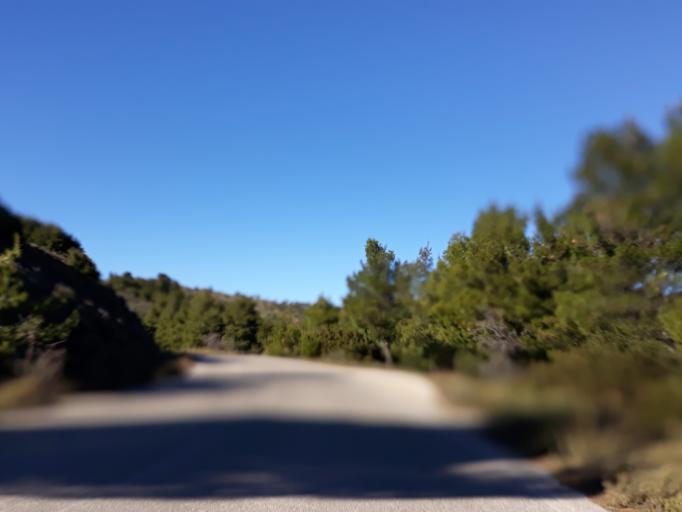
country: GR
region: Attica
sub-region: Nomarchia Dytikis Attikis
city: Fyli
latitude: 38.1214
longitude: 23.6498
